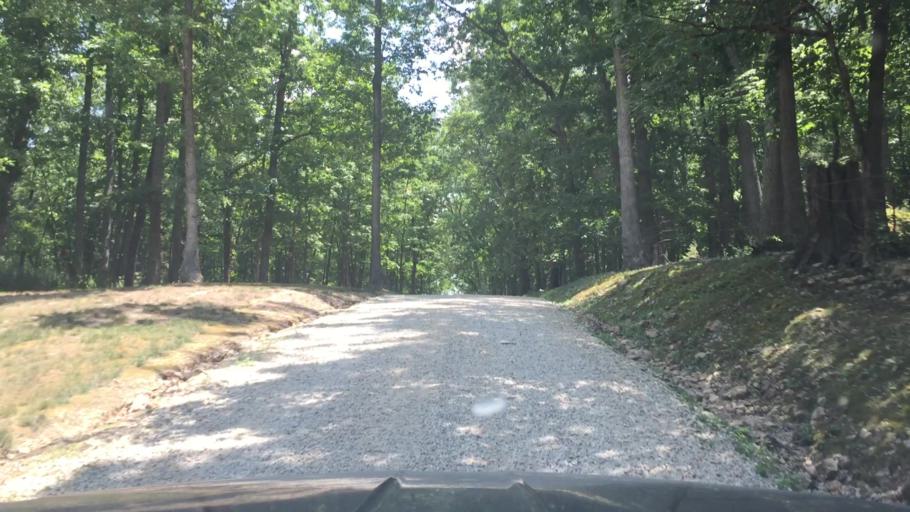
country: US
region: Missouri
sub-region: Miller County
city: Tuscumbia
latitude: 38.1310
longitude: -92.4425
